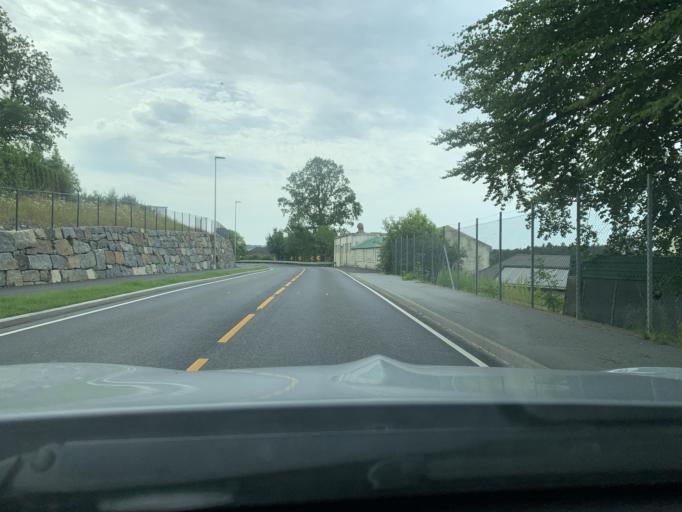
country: NO
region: Rogaland
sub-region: Sandnes
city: Sandnes
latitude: 58.7778
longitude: 5.7205
